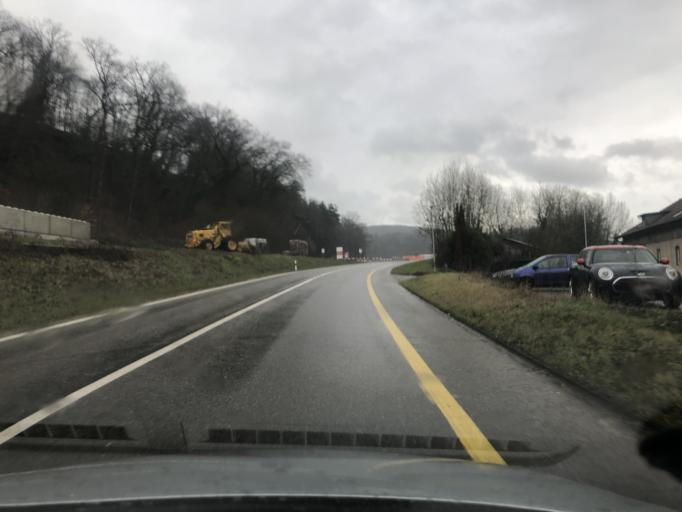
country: CH
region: Aargau
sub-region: Bezirk Zurzach
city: Koblenz
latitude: 47.5968
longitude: 8.2287
